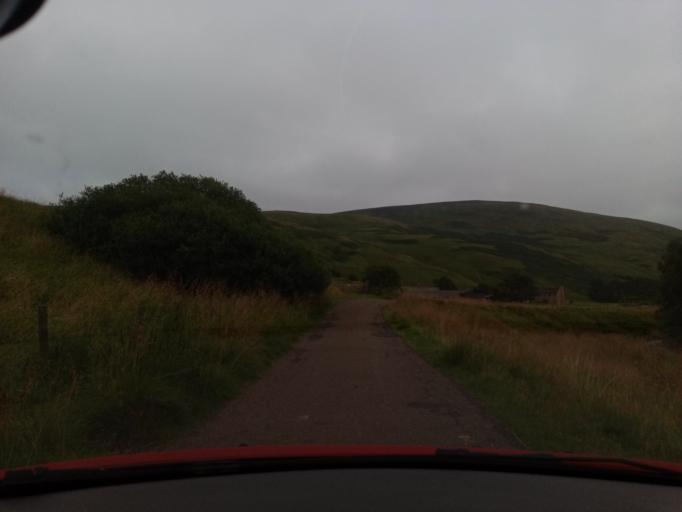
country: GB
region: England
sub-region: Northumberland
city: Rochester
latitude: 55.3921
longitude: -2.2128
